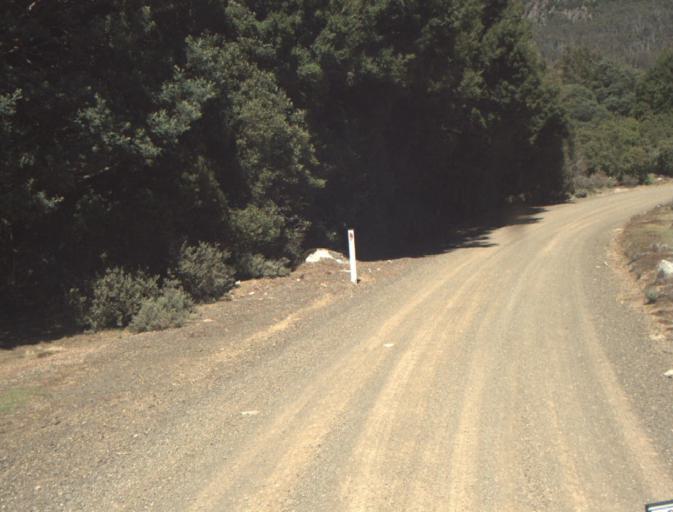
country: AU
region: Tasmania
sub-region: Dorset
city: Scottsdale
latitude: -41.3643
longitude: 147.4316
